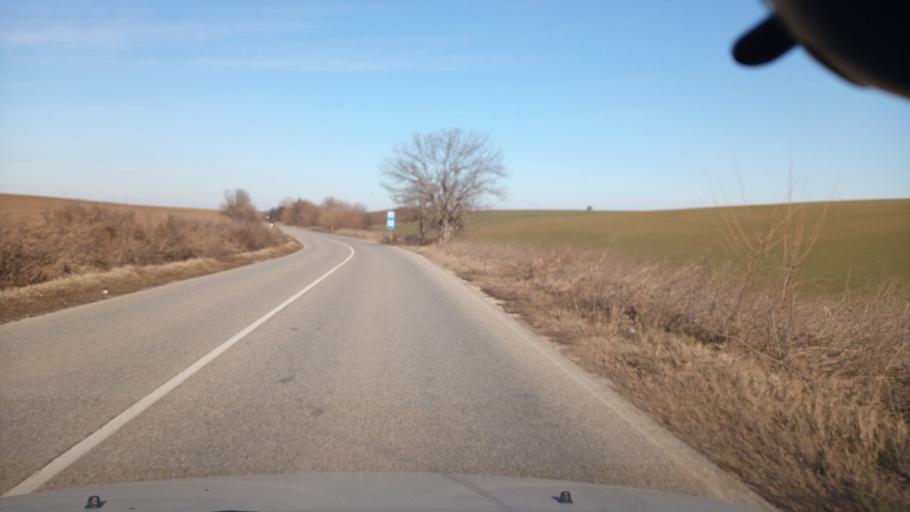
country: BG
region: Pleven
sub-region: Obshtina Pleven
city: Pleven
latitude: 43.4498
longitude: 24.7263
